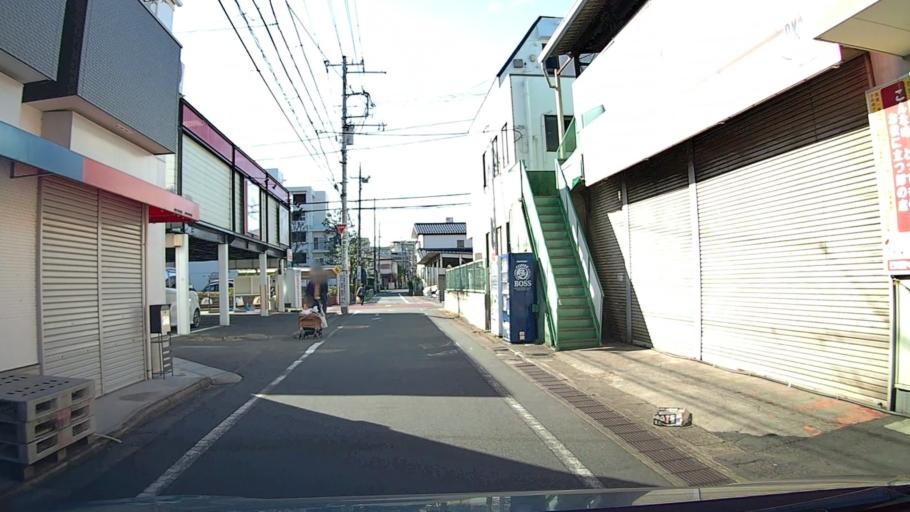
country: JP
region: Saitama
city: Wako
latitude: 35.7455
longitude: 139.6191
